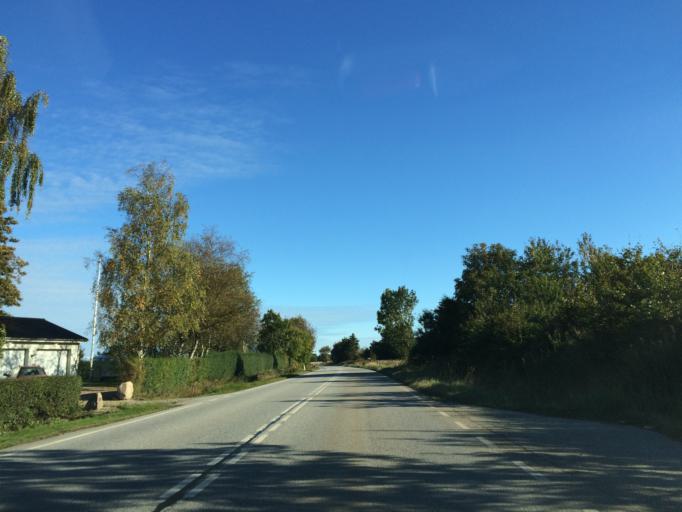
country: DK
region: Central Jutland
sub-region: Randers Kommune
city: Randers
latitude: 56.4011
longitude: 9.9926
